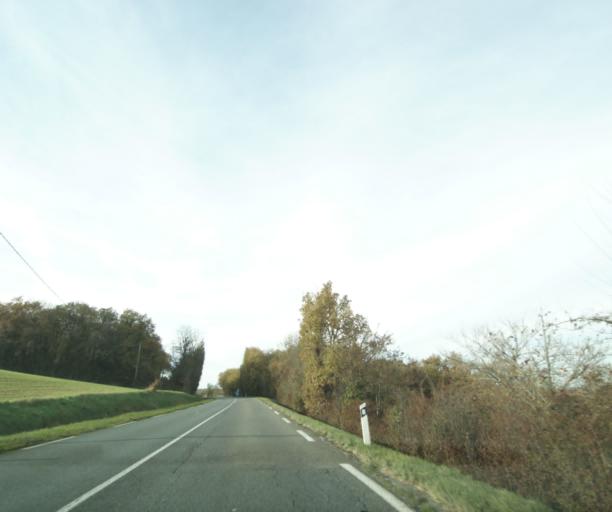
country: FR
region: Midi-Pyrenees
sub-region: Departement du Gers
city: Gimont
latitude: 43.6103
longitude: 0.9575
